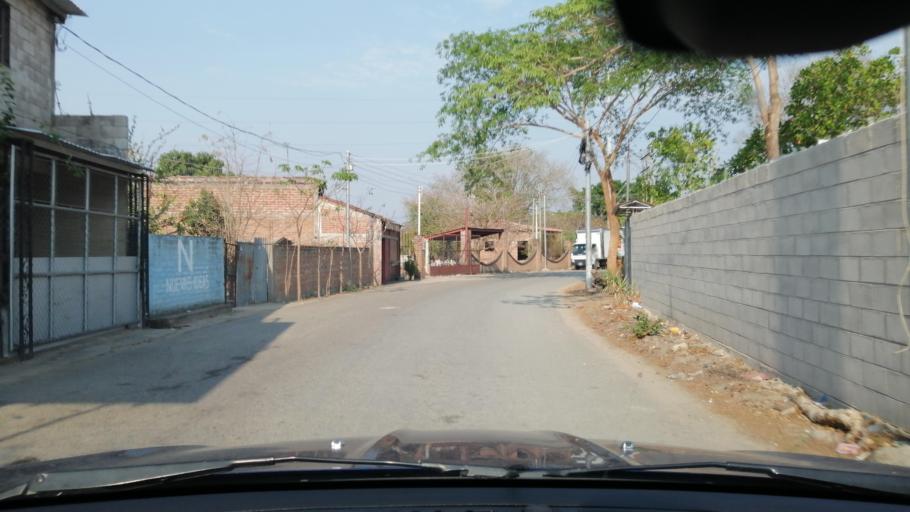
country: SV
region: Santa Ana
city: Metapan
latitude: 14.2319
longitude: -89.4658
